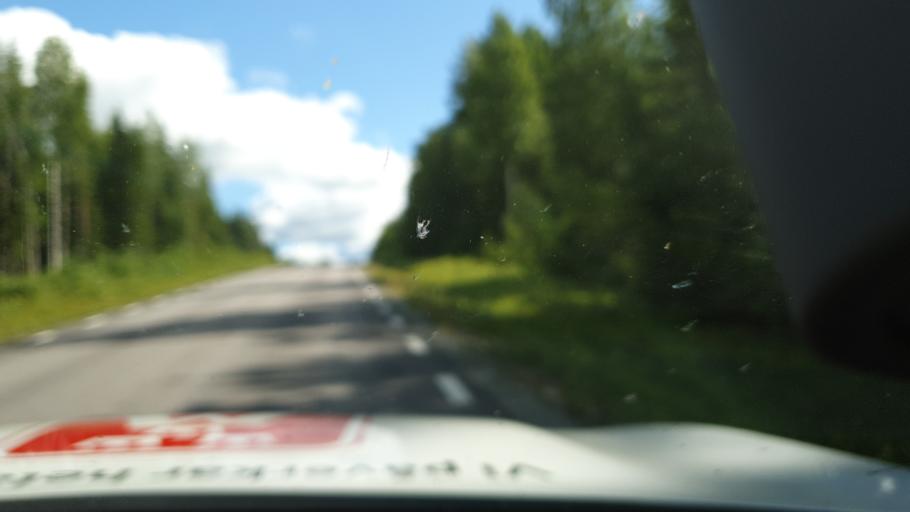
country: SE
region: Vaesterbotten
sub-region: Mala Kommun
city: Mala
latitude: 65.0576
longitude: 18.5577
